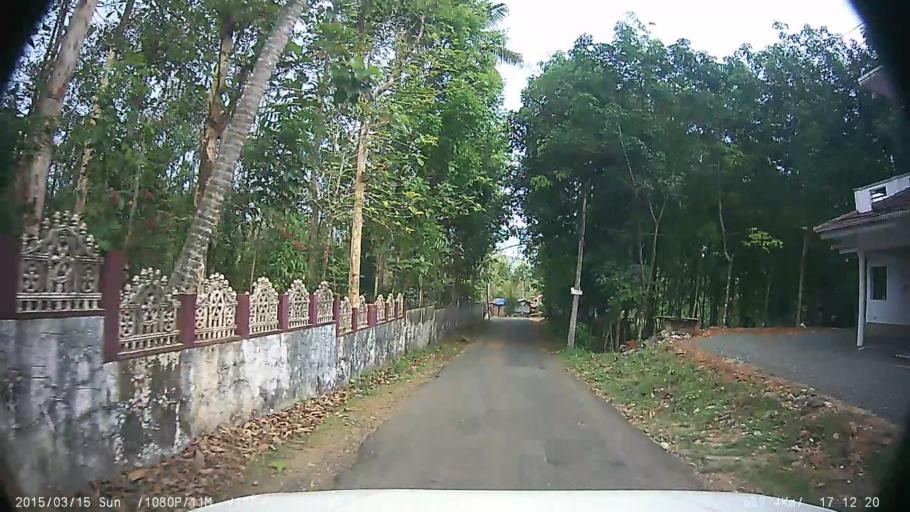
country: IN
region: Kerala
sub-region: Kottayam
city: Palackattumala
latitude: 9.8561
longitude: 76.6801
